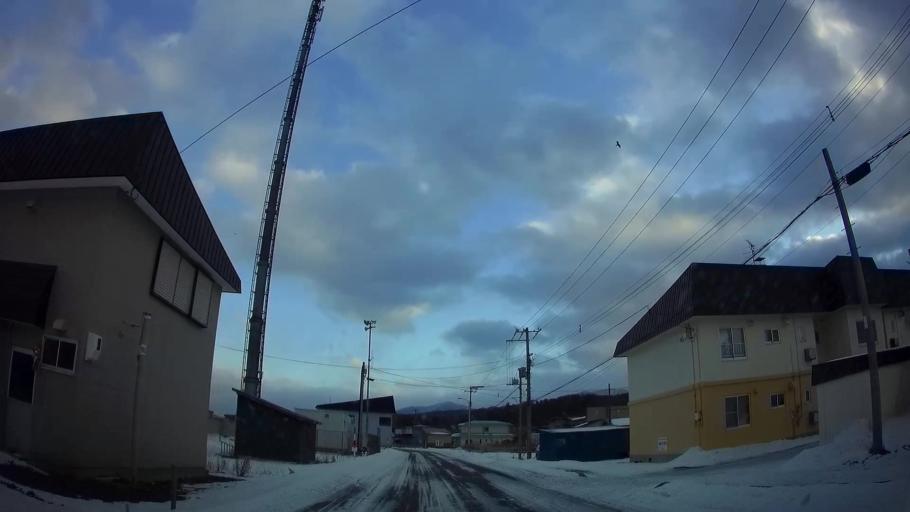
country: JP
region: Hokkaido
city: Nanae
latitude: 42.0346
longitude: 140.8205
